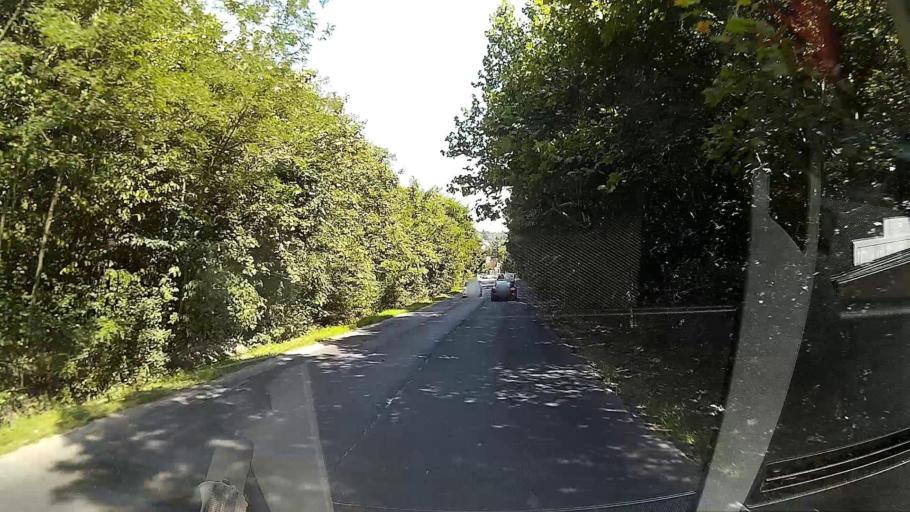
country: HU
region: Pest
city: Budakeszi
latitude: 47.5440
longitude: 18.9516
